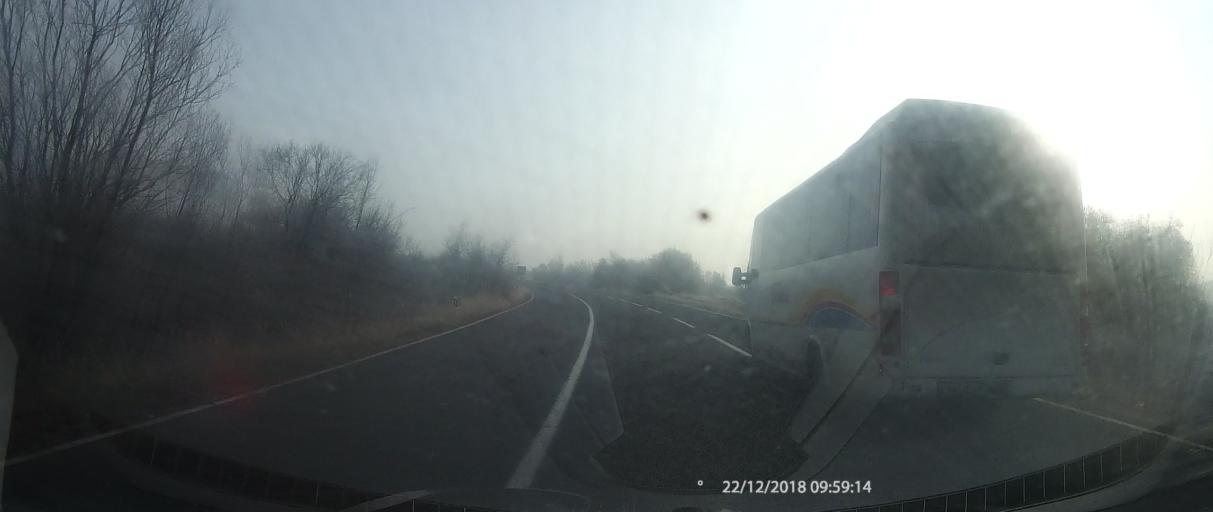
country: MK
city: Klechovce
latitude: 42.1519
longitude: 21.9546
